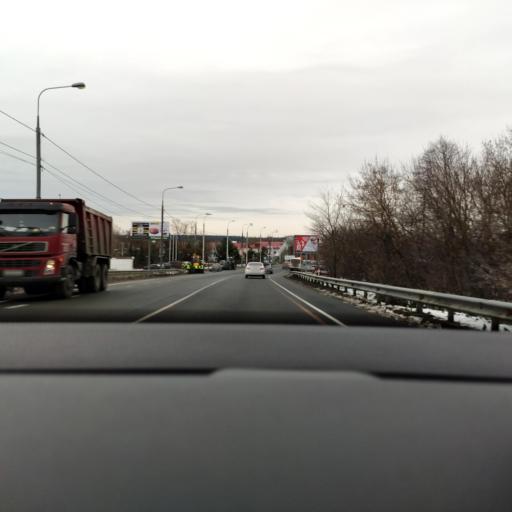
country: RU
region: Moskovskaya
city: Zvenigorod
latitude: 55.7296
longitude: 36.8680
